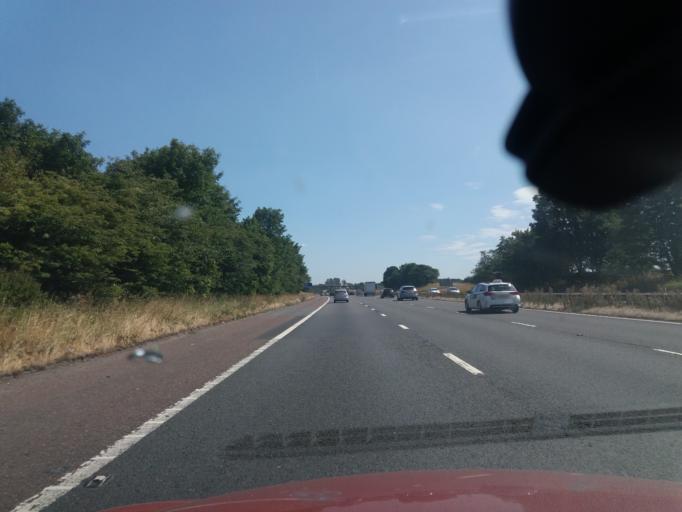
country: GB
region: England
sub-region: Borough of Bolton
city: Horwich
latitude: 53.5828
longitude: -2.5552
